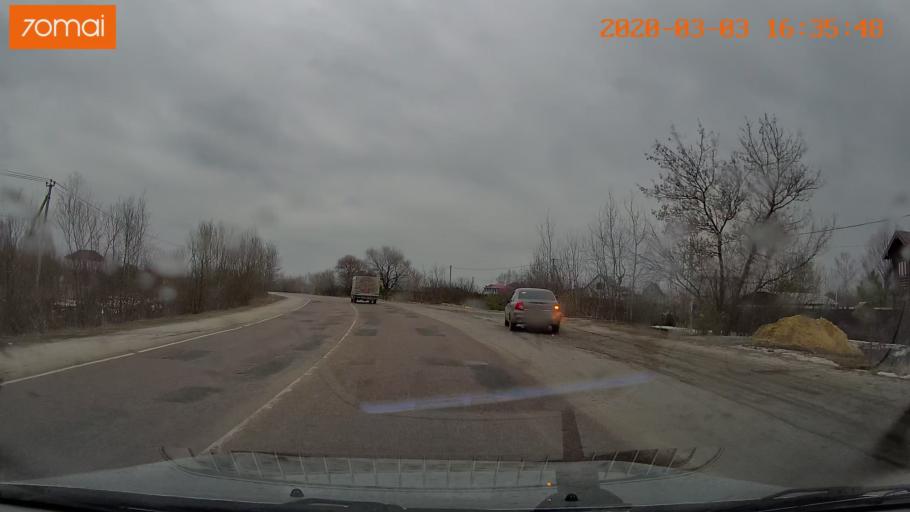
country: RU
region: Moskovskaya
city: Lopatinskiy
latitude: 55.4024
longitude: 38.7658
